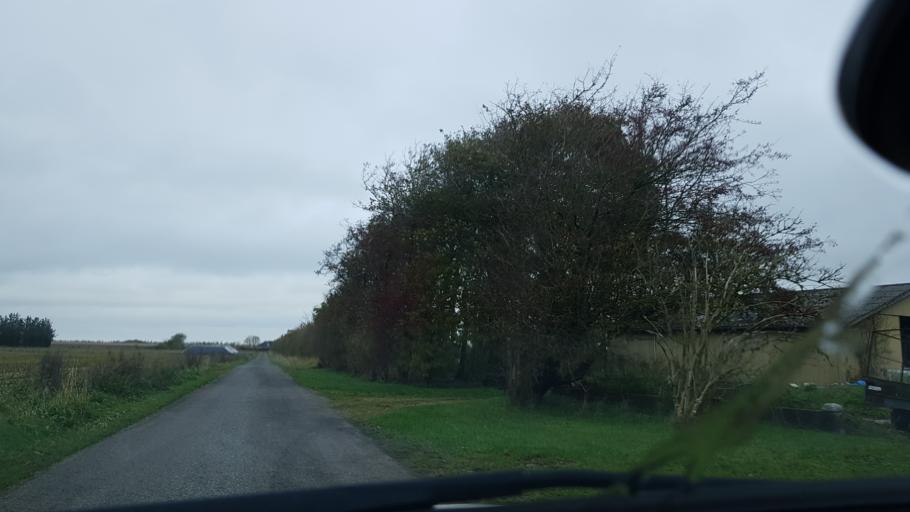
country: DK
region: South Denmark
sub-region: Esbjerg Kommune
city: Ribe
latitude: 55.2565
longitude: 8.8372
